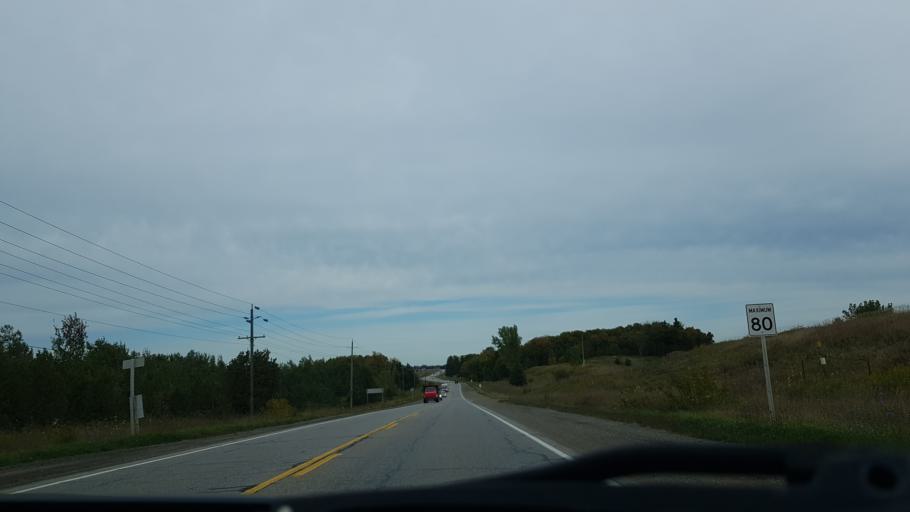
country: CA
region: Ontario
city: Orangeville
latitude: 43.8119
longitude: -80.0488
